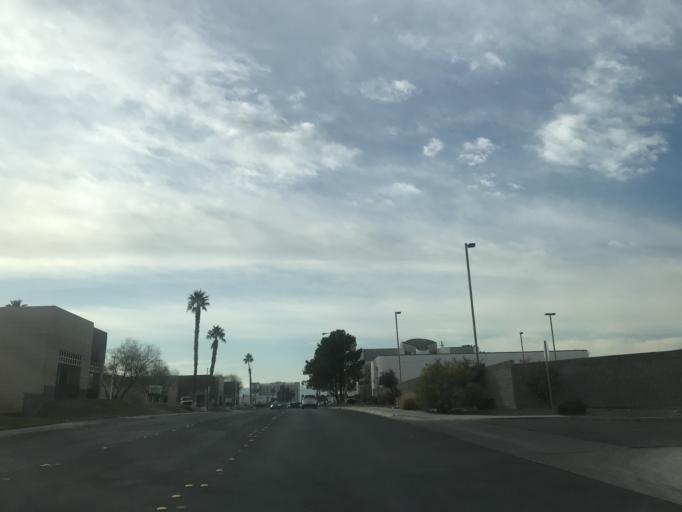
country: US
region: Nevada
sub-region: Clark County
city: Paradise
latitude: 36.1046
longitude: -115.1835
